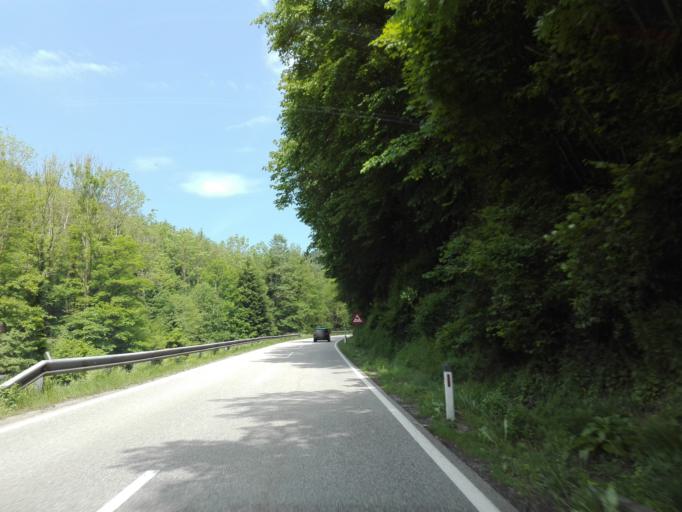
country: AT
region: Upper Austria
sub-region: Politischer Bezirk Rohrbach
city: Kleinzell im Muehlkreis
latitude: 48.3838
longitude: 13.9427
